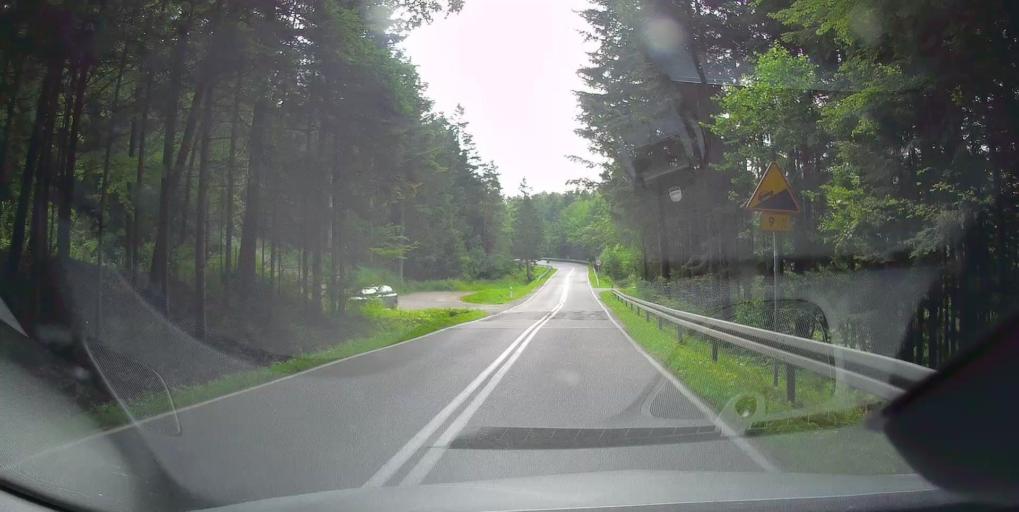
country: PL
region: Lesser Poland Voivodeship
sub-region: Powiat tarnowski
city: Zakliczyn
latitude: 49.7709
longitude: 20.7750
